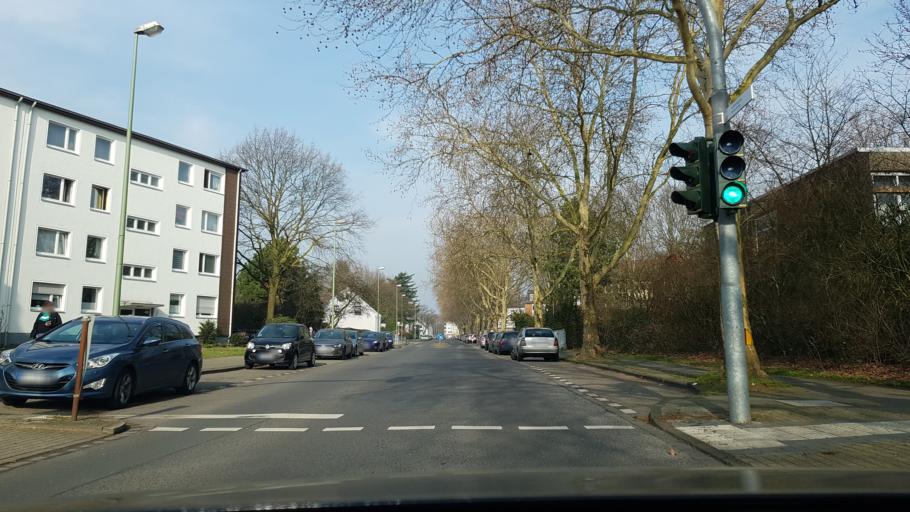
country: DE
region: North Rhine-Westphalia
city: Meiderich
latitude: 51.5126
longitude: 6.7895
